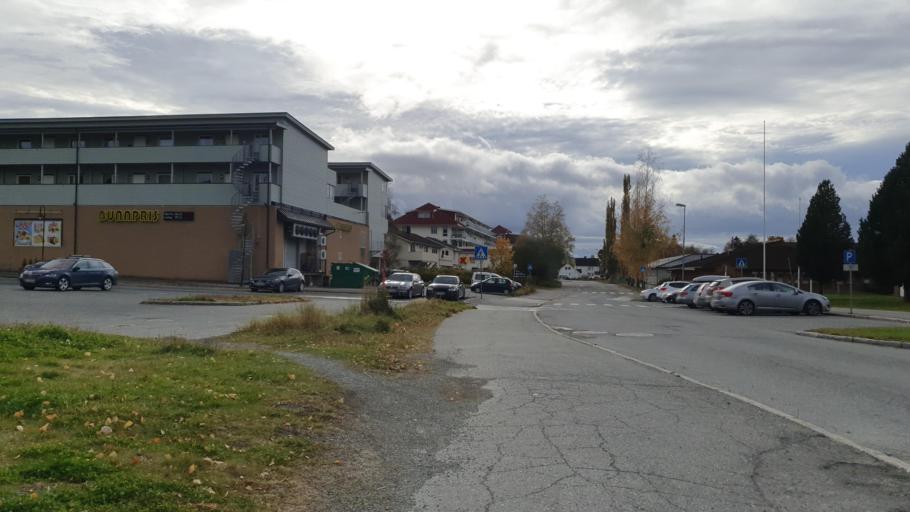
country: NO
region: Sor-Trondelag
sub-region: Klaebu
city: Klaebu
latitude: 63.3009
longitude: 10.4835
